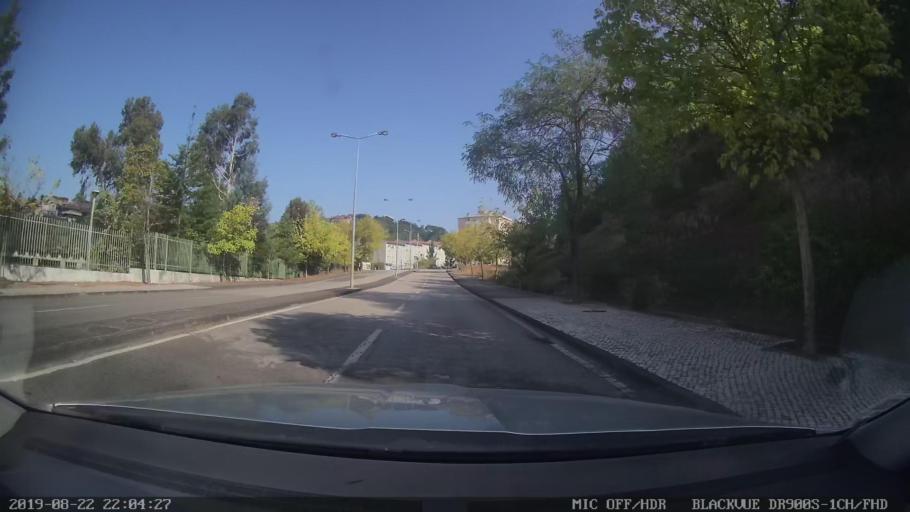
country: PT
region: Coimbra
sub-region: Coimbra
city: Coimbra
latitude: 40.2087
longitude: -8.4016
